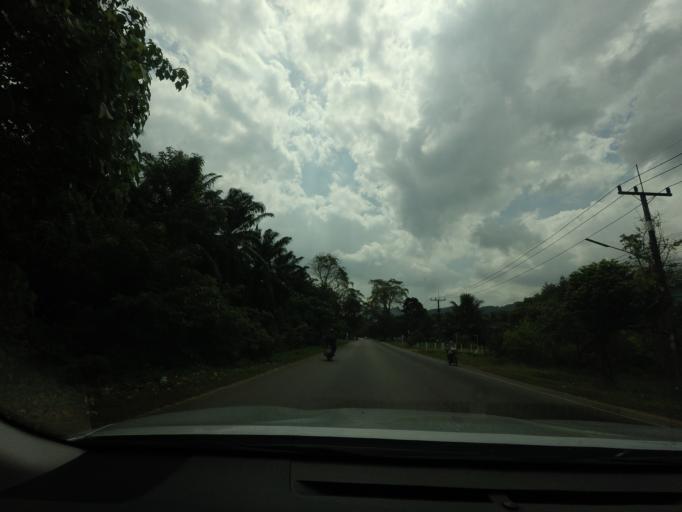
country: TH
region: Phangnga
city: Ban Ao Nang
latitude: 8.1149
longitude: 98.8022
